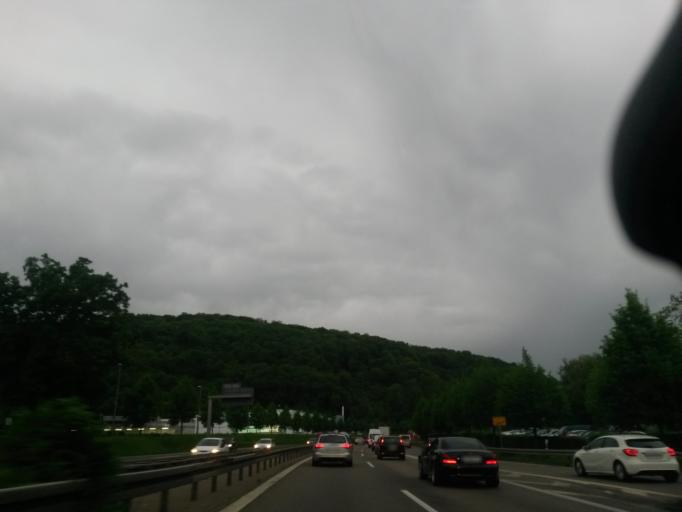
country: DE
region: Baden-Wuerttemberg
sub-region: Regierungsbezirk Stuttgart
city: Ostfildern
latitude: 48.7410
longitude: 9.2734
